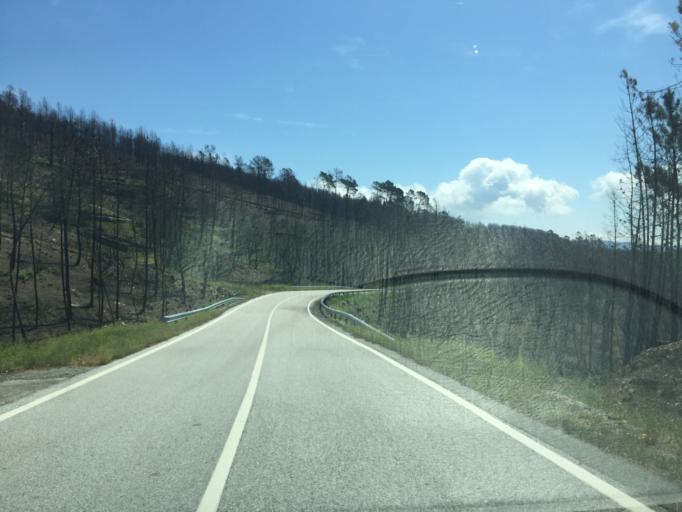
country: PT
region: Coimbra
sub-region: Pampilhosa da Serra
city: Pampilhosa da Serra
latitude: 40.0072
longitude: -7.9828
